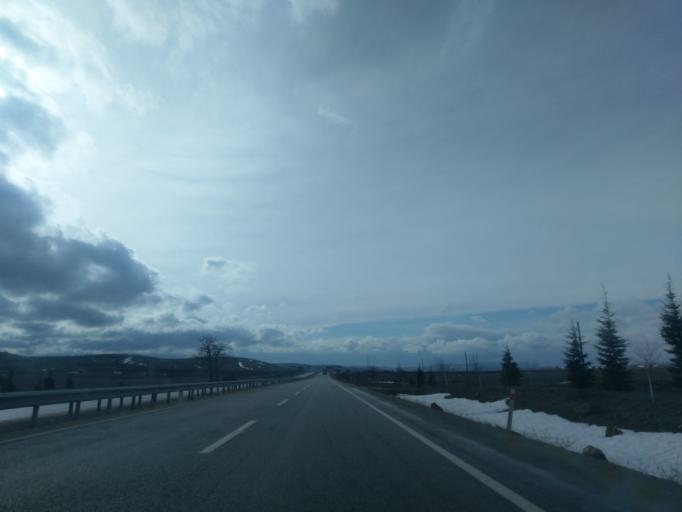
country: TR
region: Eskisehir
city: Inonu
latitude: 39.7117
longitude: 30.1728
